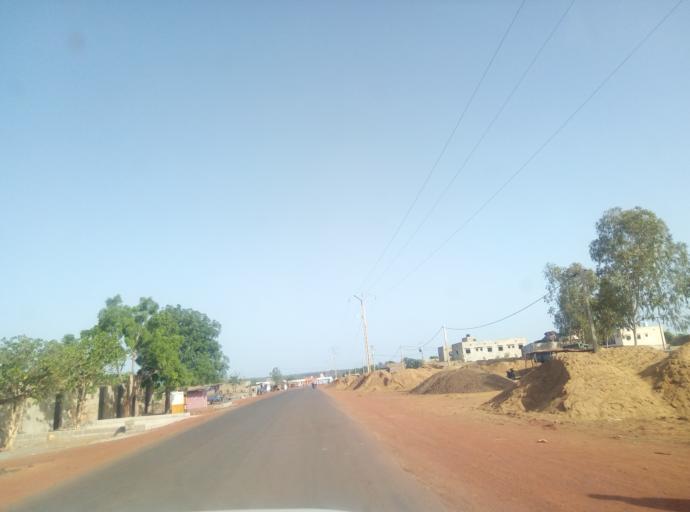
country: ML
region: Bamako
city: Bamako
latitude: 12.5997
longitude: -7.7686
